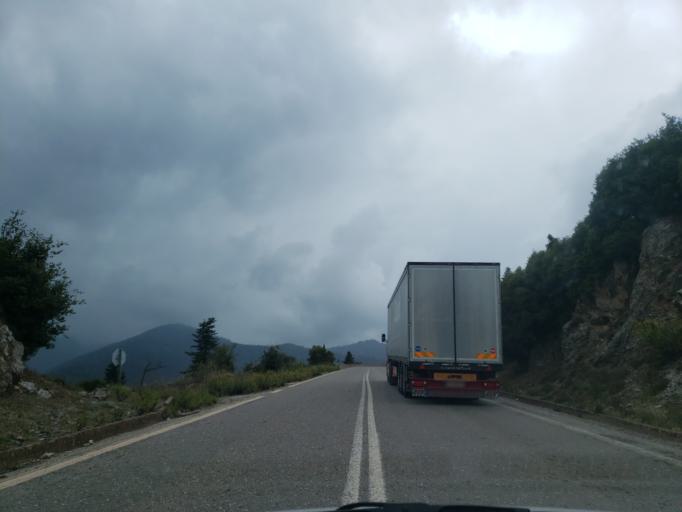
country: GR
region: Central Greece
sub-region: Nomos Fokidos
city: Amfissa
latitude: 38.6422
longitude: 22.3948
